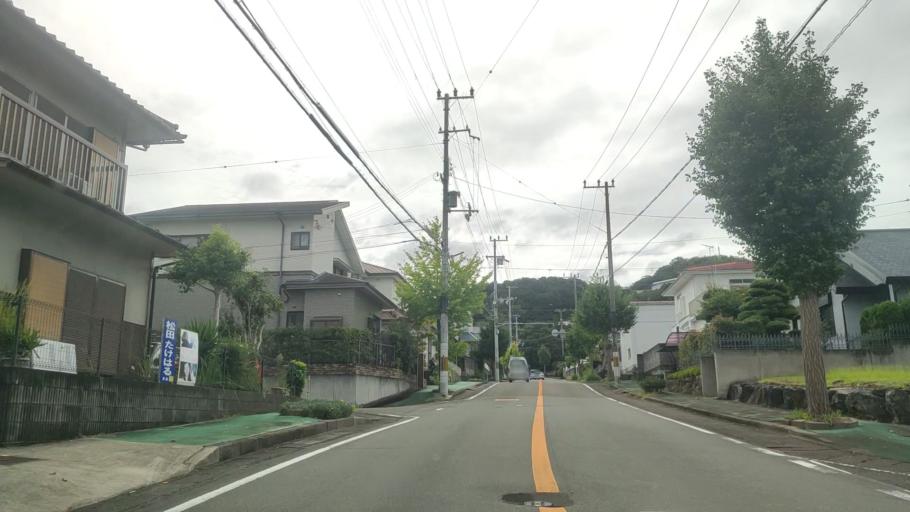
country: JP
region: Wakayama
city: Tanabe
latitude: 33.6761
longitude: 135.3762
